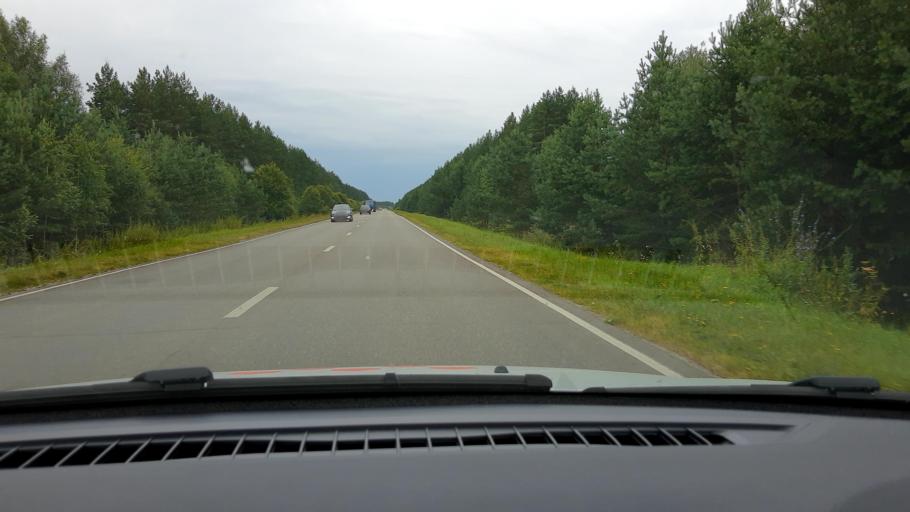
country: RU
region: Nizjnij Novgorod
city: Vyyezdnoye
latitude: 55.2047
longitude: 43.6234
